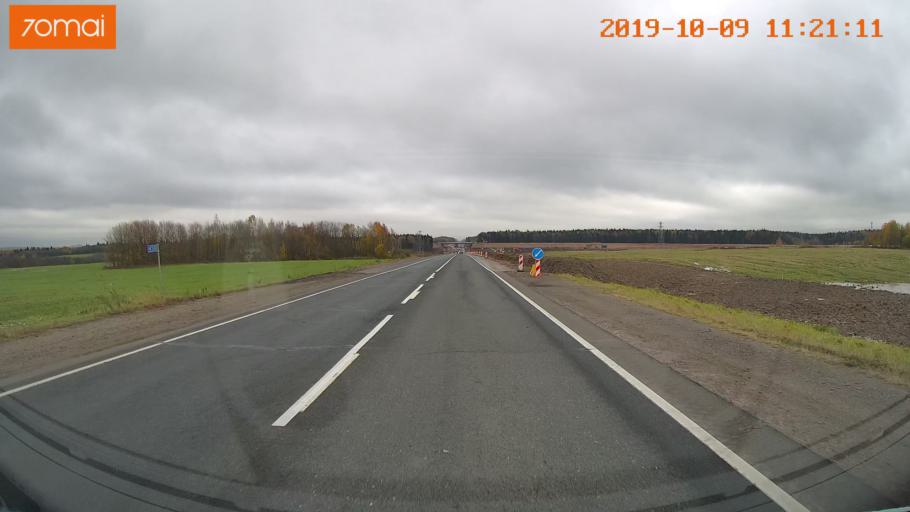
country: RU
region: Vologda
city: Vologda
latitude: 59.1416
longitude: 39.9472
